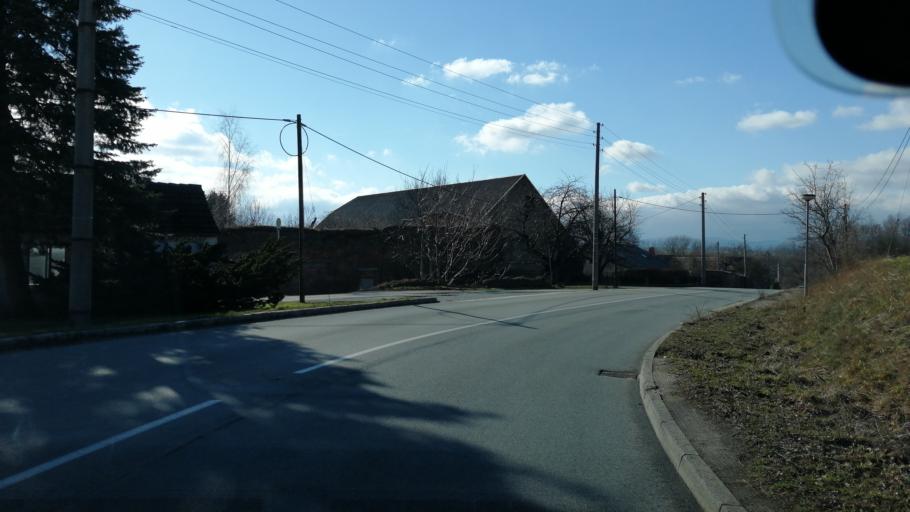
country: DE
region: Saxony
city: Lobau
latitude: 51.1480
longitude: 14.7174
